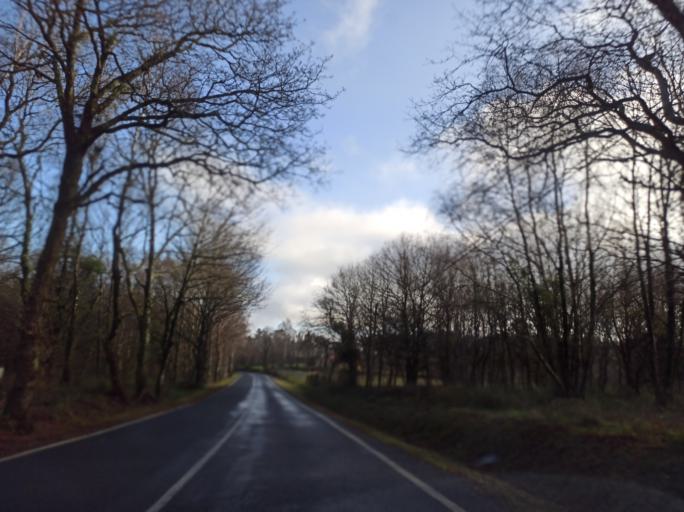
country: ES
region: Galicia
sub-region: Provincia da Coruna
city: Sobrado
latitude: 43.0789
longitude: -8.0074
